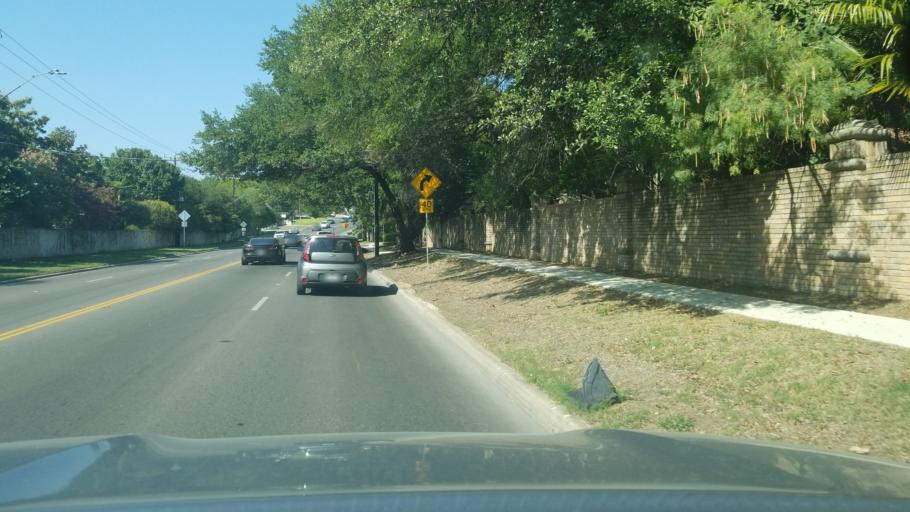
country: US
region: Texas
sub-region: Bexar County
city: Hollywood Park
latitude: 29.5793
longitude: -98.5090
